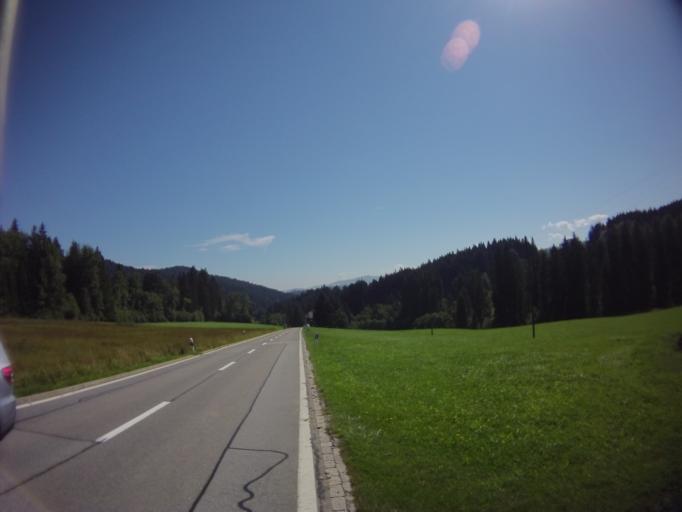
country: CH
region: Schwyz
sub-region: Bezirk Hoefe
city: Schindellegi
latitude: 47.1466
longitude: 8.6859
